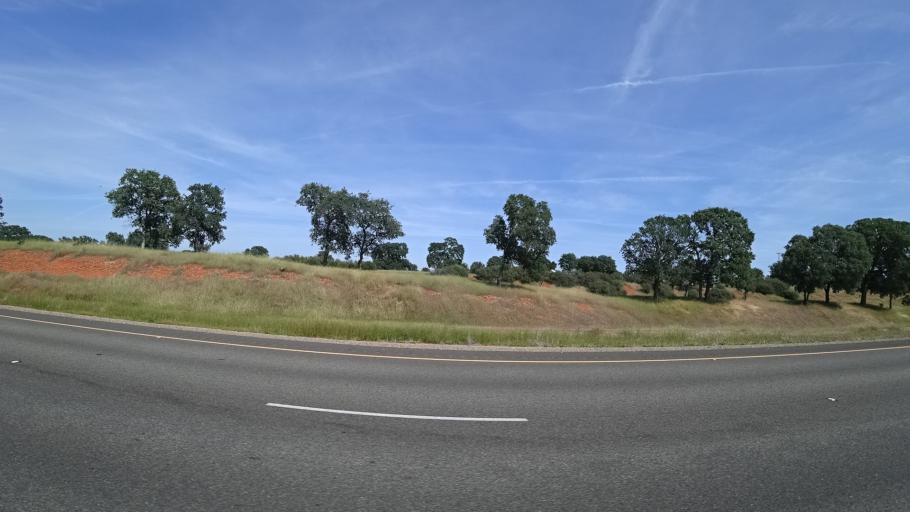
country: US
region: California
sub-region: Shasta County
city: Cottonwood
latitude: 40.3396
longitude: -122.2823
